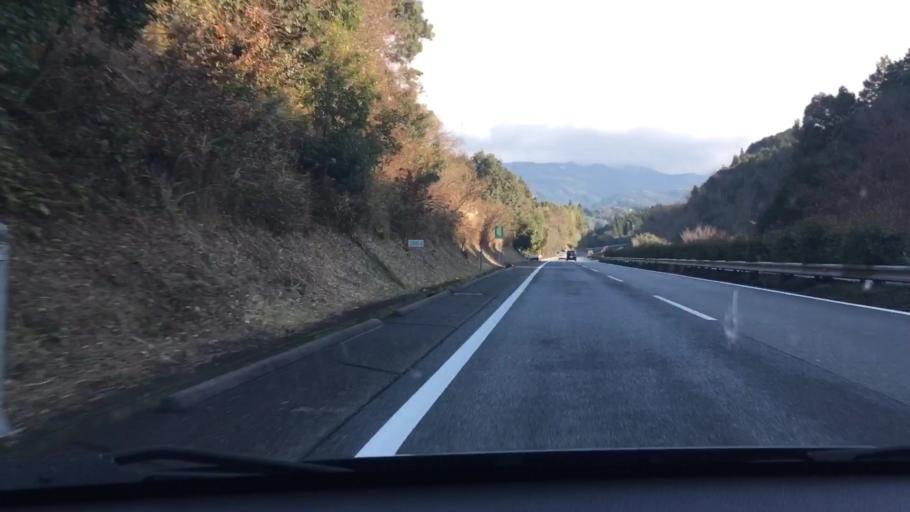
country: JP
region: Kumamoto
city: Hitoyoshi
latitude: 32.1816
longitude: 130.7826
